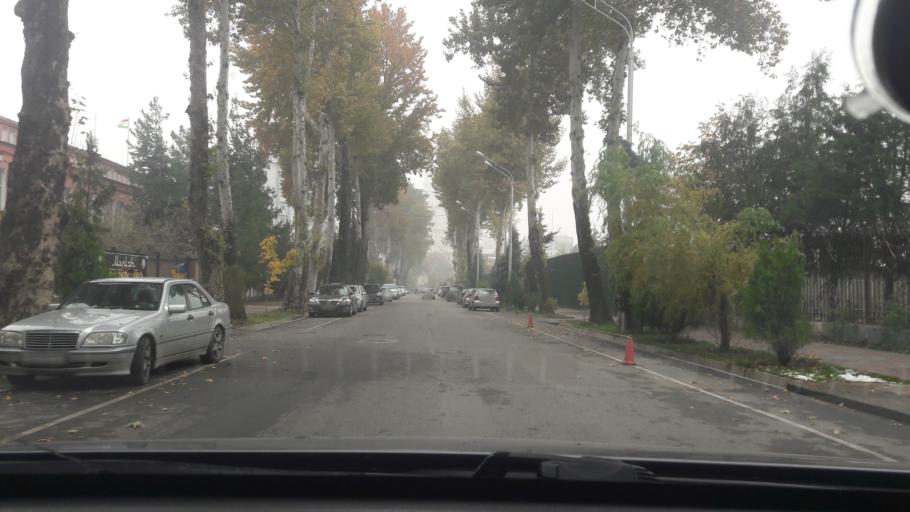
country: TJ
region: Dushanbe
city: Dushanbe
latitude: 38.5773
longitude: 68.7894
